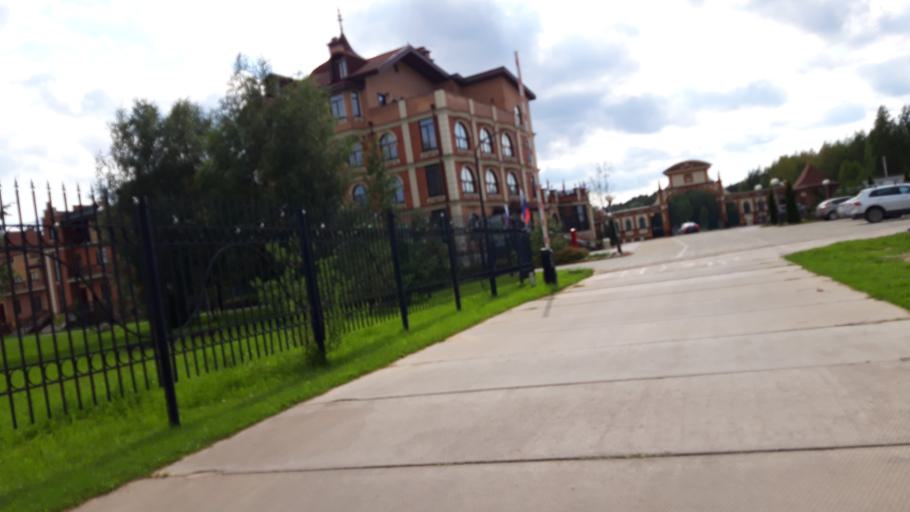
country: RU
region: Tverskaya
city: Konakovo
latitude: 56.6767
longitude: 36.7128
